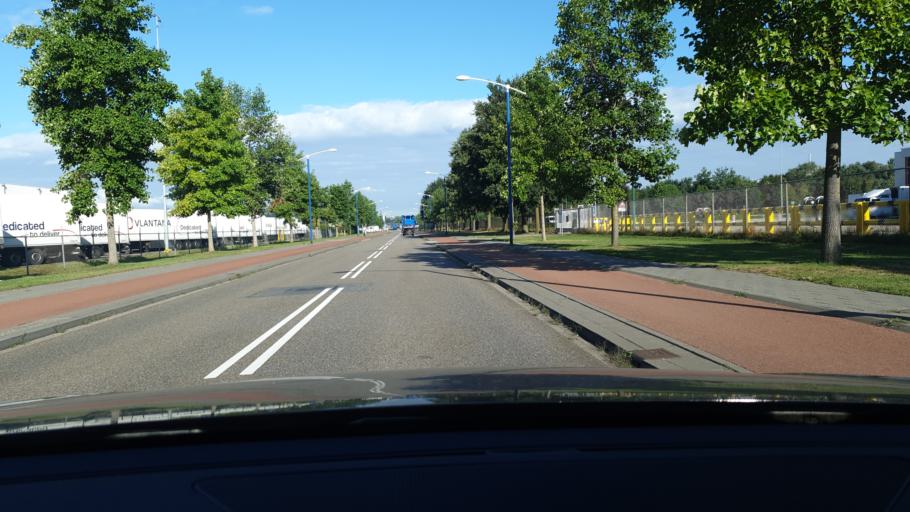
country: NL
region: North Brabant
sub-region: Gemeente Veghel
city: Eerde
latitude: 51.6107
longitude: 5.5149
